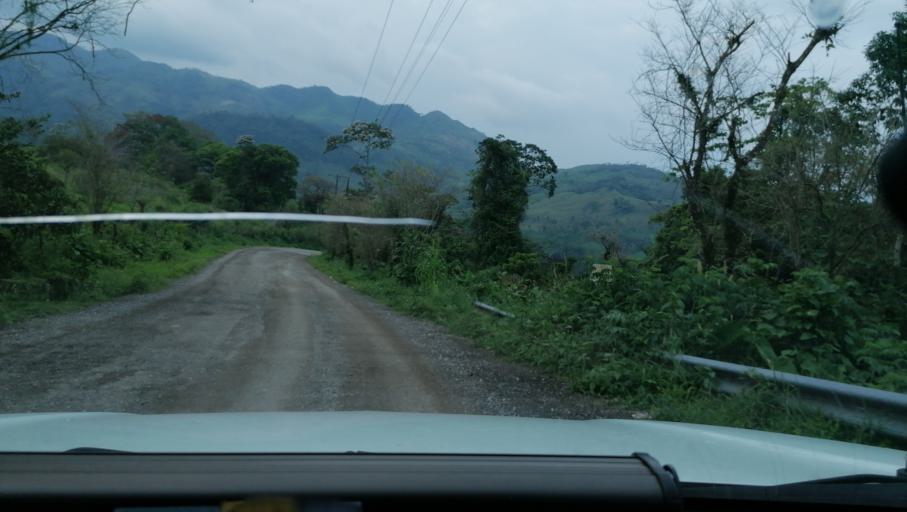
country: MX
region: Chiapas
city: Ixtacomitan
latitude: 17.3468
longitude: -93.1308
